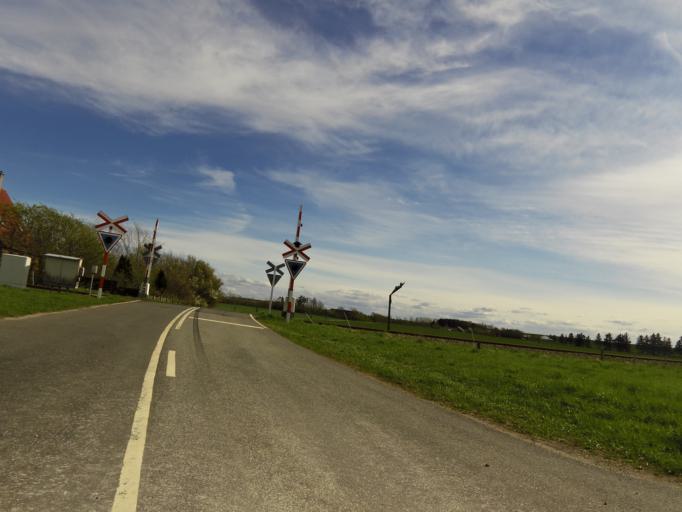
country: DK
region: Central Jutland
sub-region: Skive Kommune
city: Skive
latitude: 56.5541
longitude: 8.9592
